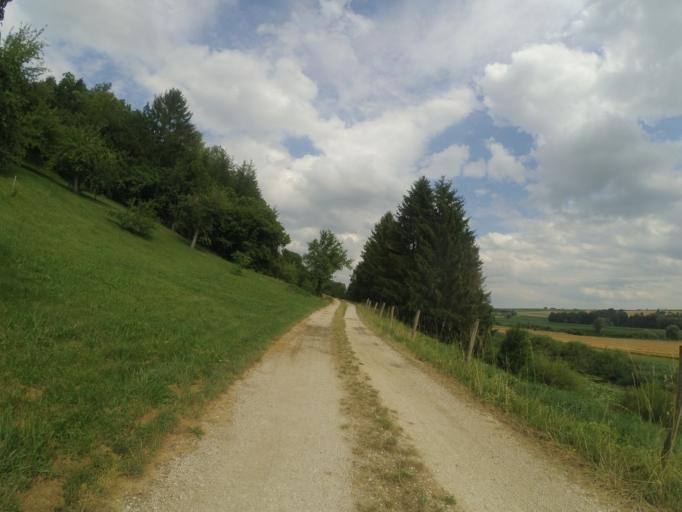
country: DE
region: Baden-Wuerttemberg
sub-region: Tuebingen Region
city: Ehingen
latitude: 48.2778
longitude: 9.7467
